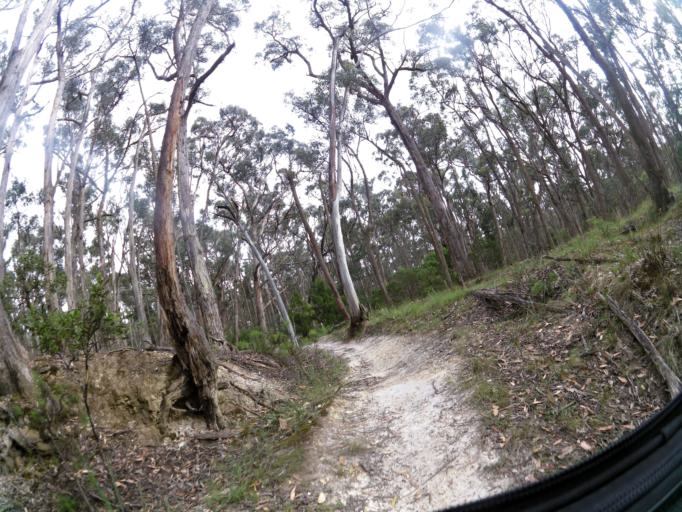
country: AU
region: Victoria
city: Brown Hill
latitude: -37.4760
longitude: 143.9121
